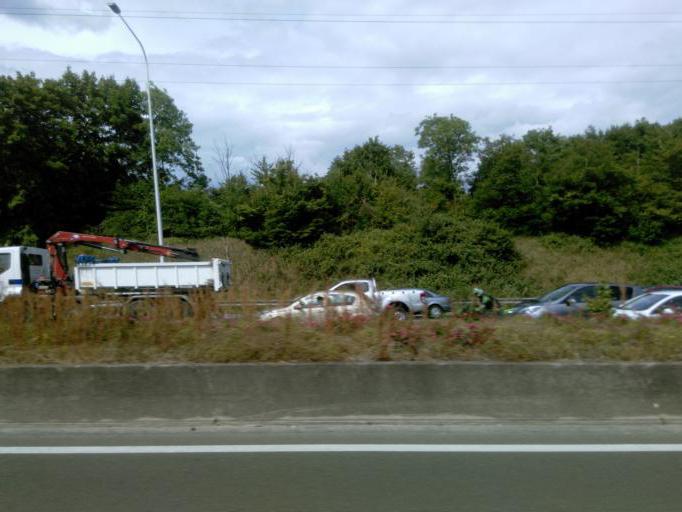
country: FR
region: Ile-de-France
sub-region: Departement du Val-d'Oise
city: Cergy-Pontoise
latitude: 49.0379
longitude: 2.0888
